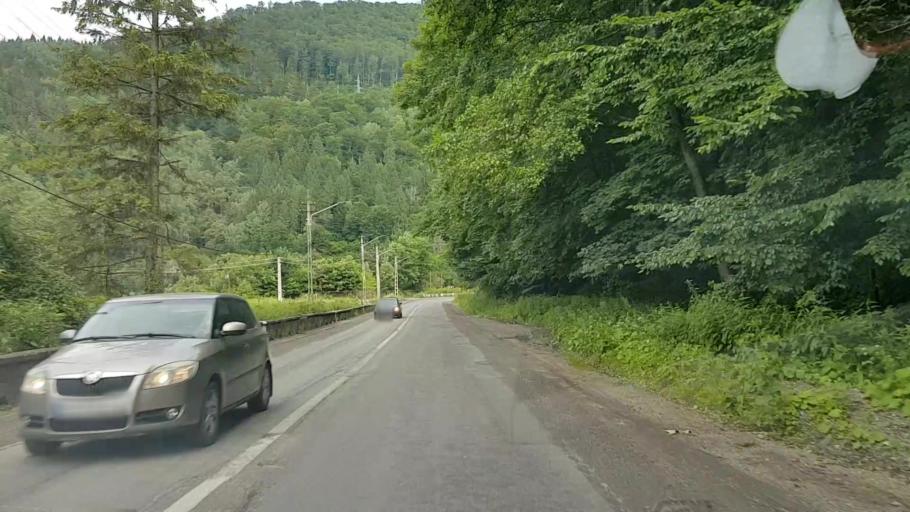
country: RO
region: Neamt
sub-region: Comuna Bicaz
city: Dodeni
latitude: 46.9353
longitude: 26.0963
